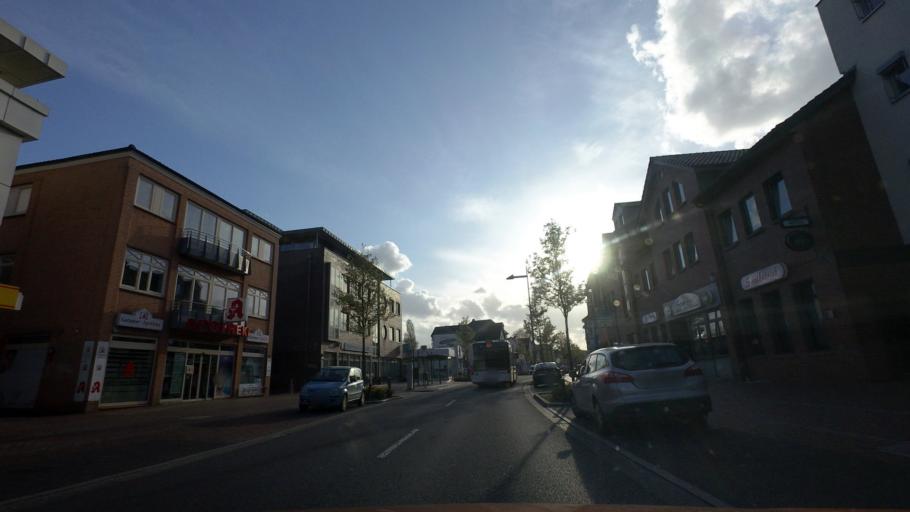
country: DE
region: Lower Saxony
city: Oldenburg
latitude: 53.1334
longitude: 8.1984
